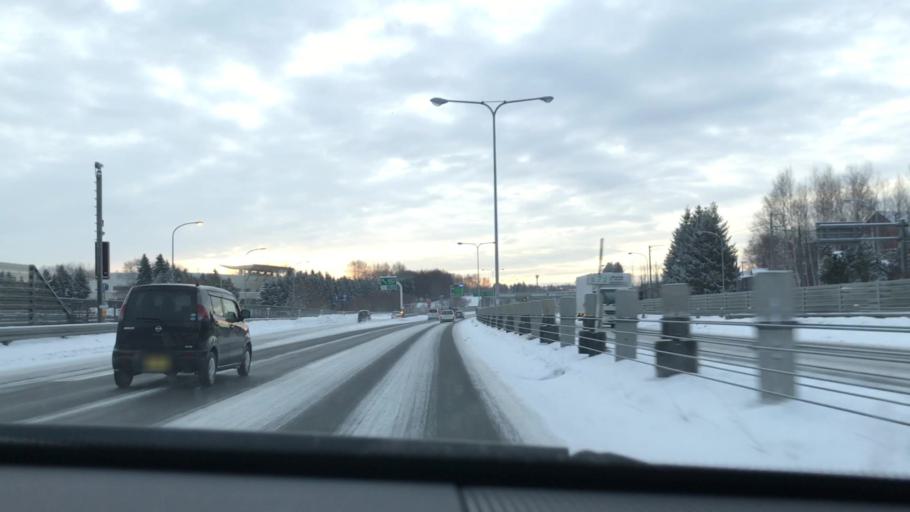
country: JP
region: Hokkaido
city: Kitahiroshima
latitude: 43.0206
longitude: 141.4597
